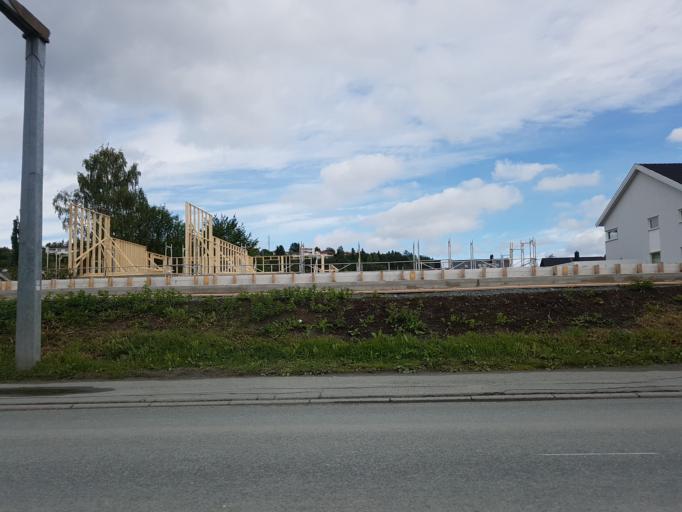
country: NO
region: Sor-Trondelag
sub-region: Trondheim
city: Trondheim
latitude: 63.4053
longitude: 10.4264
